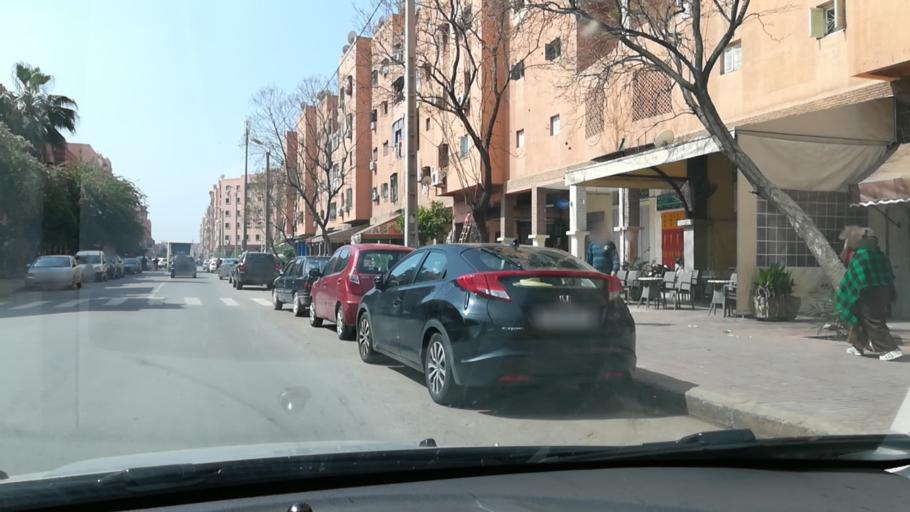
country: MA
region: Marrakech-Tensift-Al Haouz
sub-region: Marrakech
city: Marrakesh
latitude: 31.6327
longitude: -8.0625
